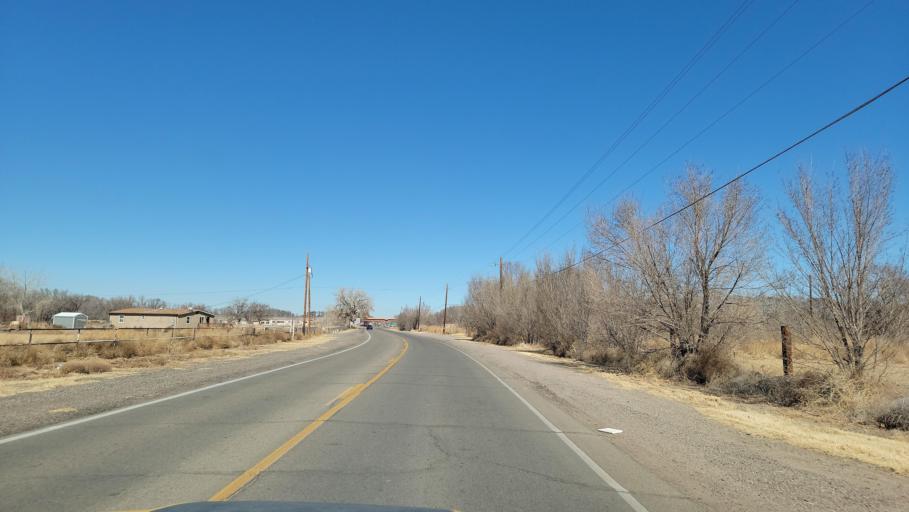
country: US
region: New Mexico
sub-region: Bernalillo County
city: South Valley
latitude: 34.9436
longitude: -106.6924
